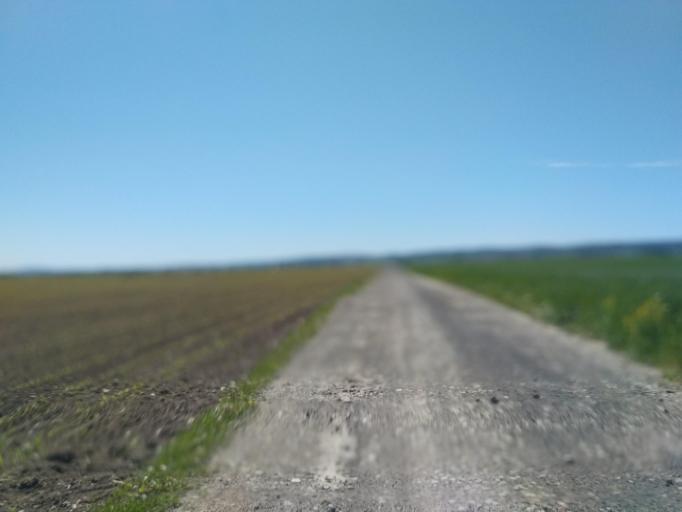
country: PL
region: Subcarpathian Voivodeship
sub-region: Powiat sanocki
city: Besko
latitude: 49.6117
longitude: 21.9746
